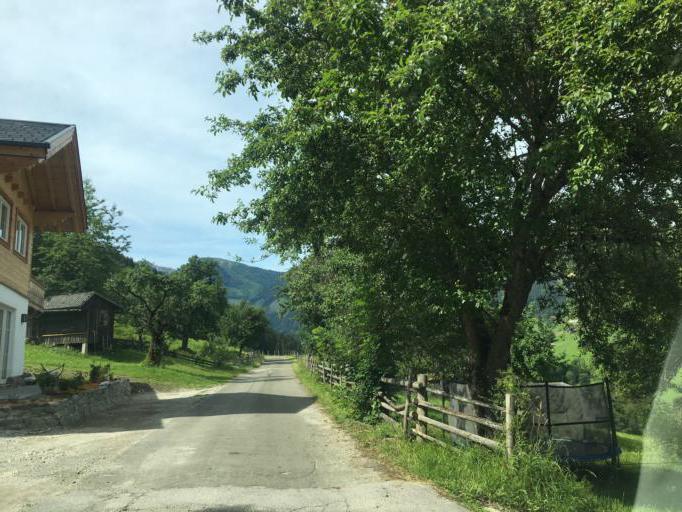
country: AT
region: Styria
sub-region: Politischer Bezirk Liezen
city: Schladming
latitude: 47.3824
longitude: 13.6855
